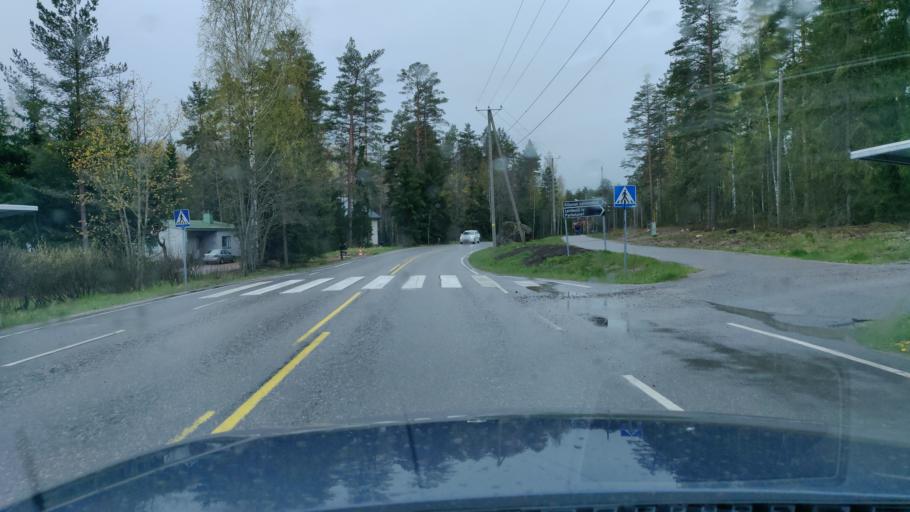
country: FI
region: Uusimaa
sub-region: Helsinki
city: Nurmijaervi
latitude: 60.5193
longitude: 24.7068
